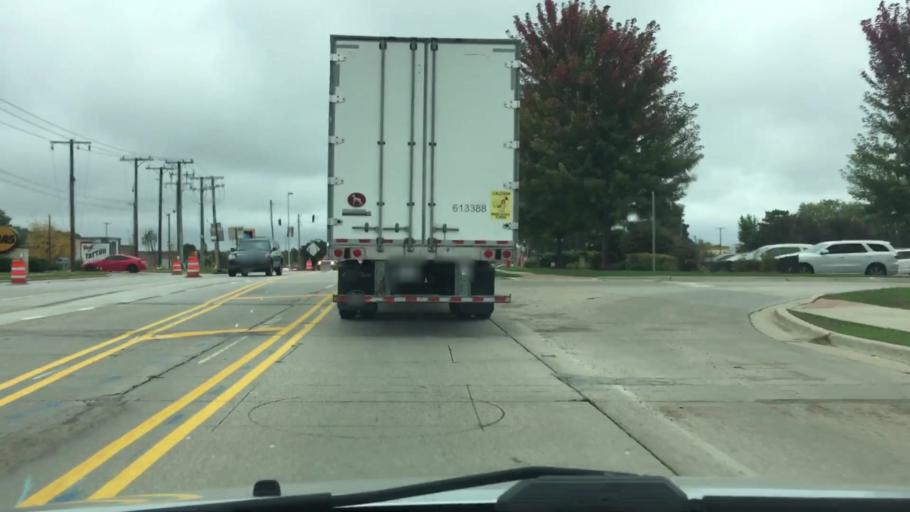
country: US
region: Illinois
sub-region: Kane County
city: West Dundee
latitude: 42.1074
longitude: -88.2933
